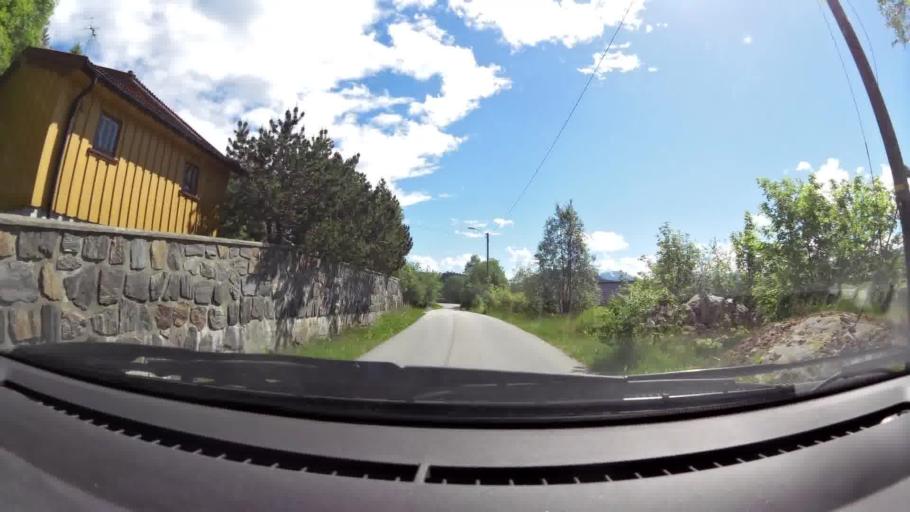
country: NO
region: More og Romsdal
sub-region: Kristiansund
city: Kristiansund
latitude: 63.0609
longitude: 7.7035
